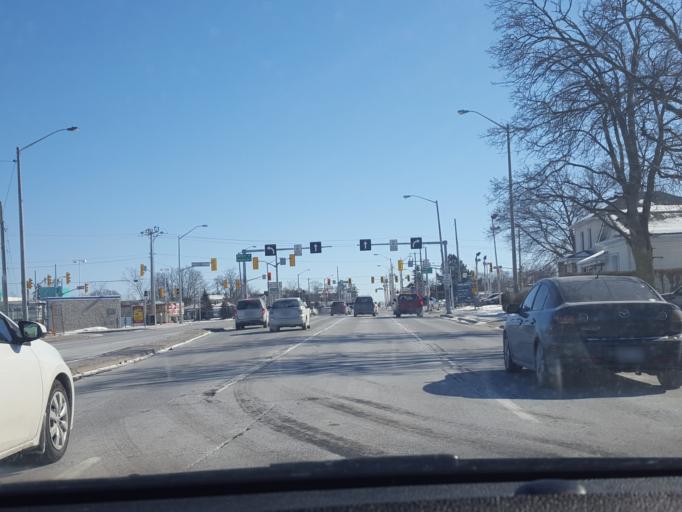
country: CA
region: Ontario
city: Cambridge
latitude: 43.3741
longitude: -80.3199
